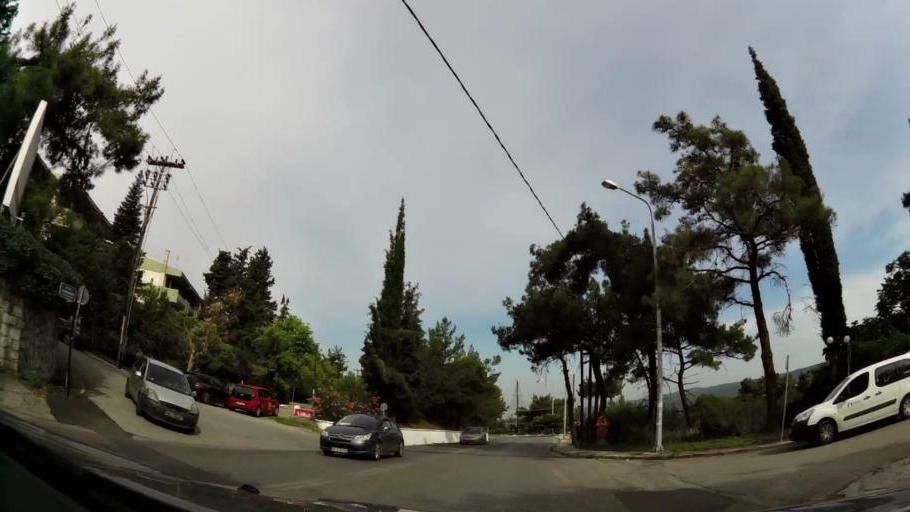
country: GR
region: Central Macedonia
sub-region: Nomos Thessalonikis
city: Panorama
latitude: 40.5920
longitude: 23.0320
